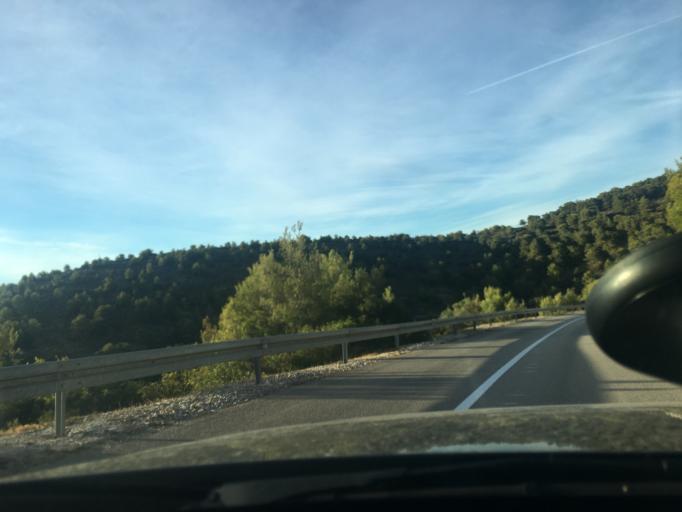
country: HR
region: Splitsko-Dalmatinska
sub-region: Grad Vis
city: Vis
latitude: 43.0569
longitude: 16.2050
